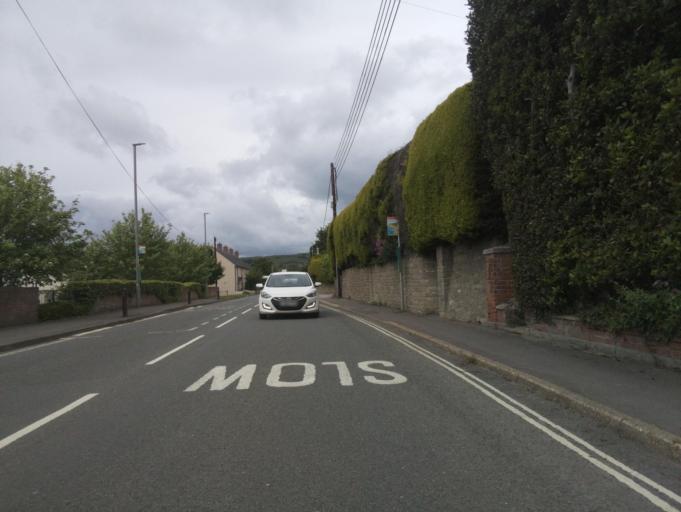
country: GB
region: England
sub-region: Dorset
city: Bridport
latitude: 50.7344
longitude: -2.7687
